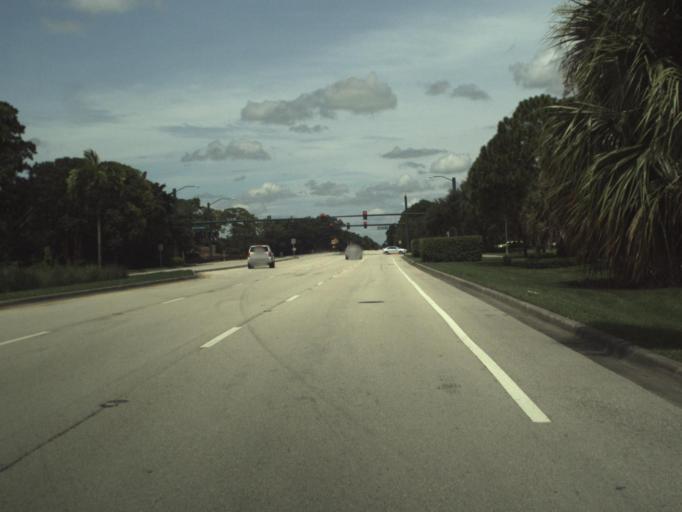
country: US
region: Florida
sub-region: Palm Beach County
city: Palm Beach Gardens
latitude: 26.8393
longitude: -80.1342
